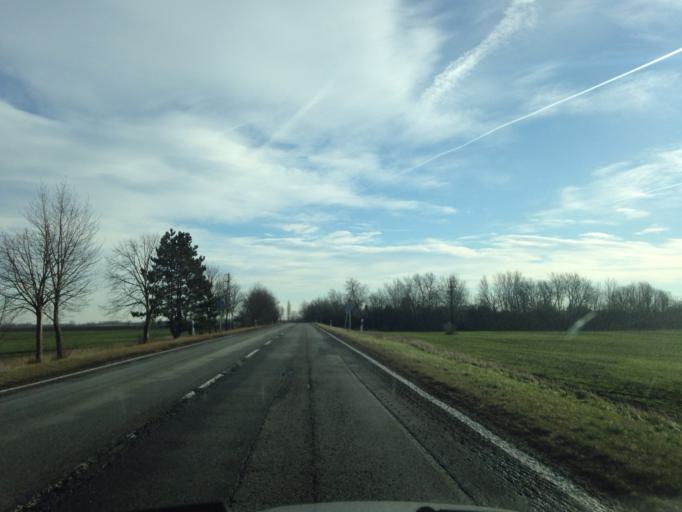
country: HU
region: Gyor-Moson-Sopron
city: Mosonszentmiklos
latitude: 47.7725
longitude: 17.4234
